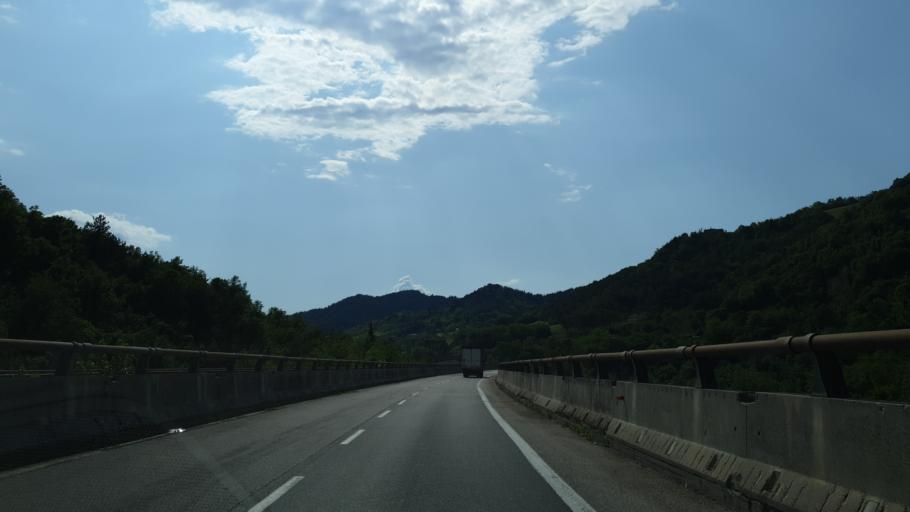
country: IT
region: Emilia-Romagna
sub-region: Forli-Cesena
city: Sarsina
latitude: 43.9127
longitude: 12.1345
